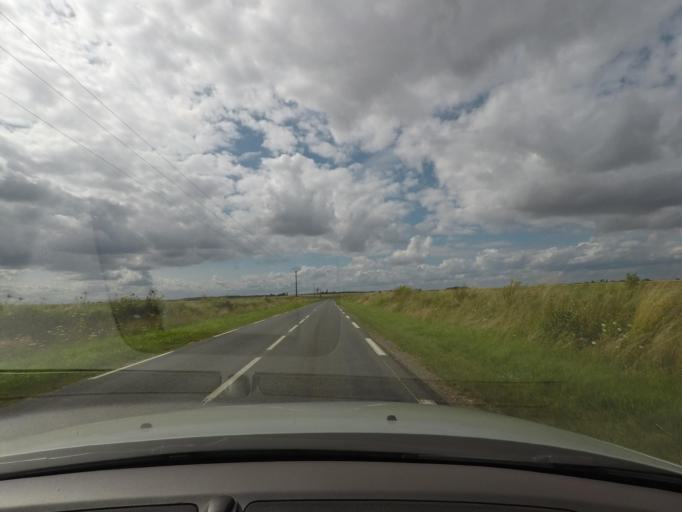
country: FR
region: Haute-Normandie
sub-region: Departement de l'Eure
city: Les Andelys
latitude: 49.2236
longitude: 1.4448
